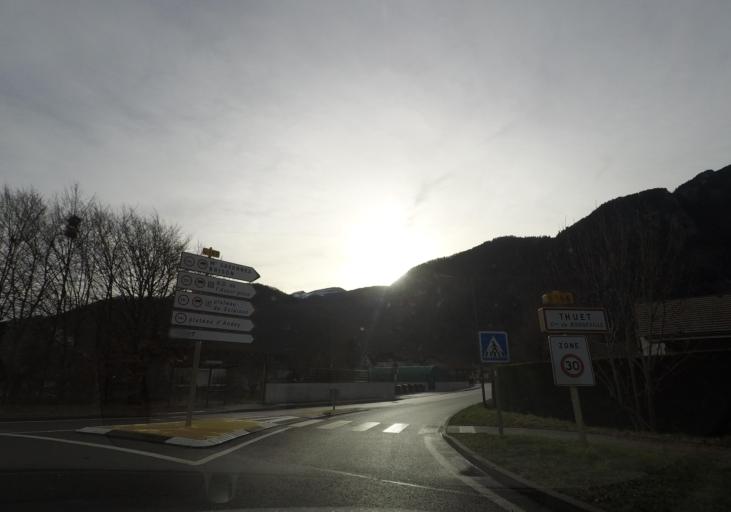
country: FR
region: Rhone-Alpes
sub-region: Departement de la Haute-Savoie
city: Ayse
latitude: 46.0691
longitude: 6.4419
